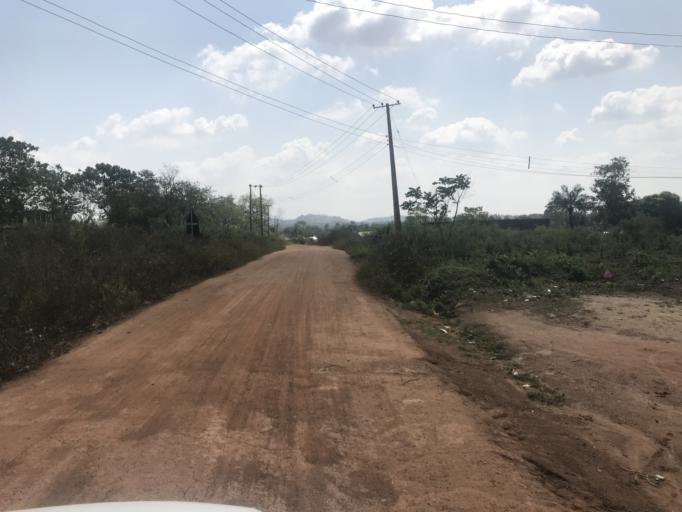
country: NG
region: Osun
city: Iragbiji
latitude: 7.8890
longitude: 4.7017
